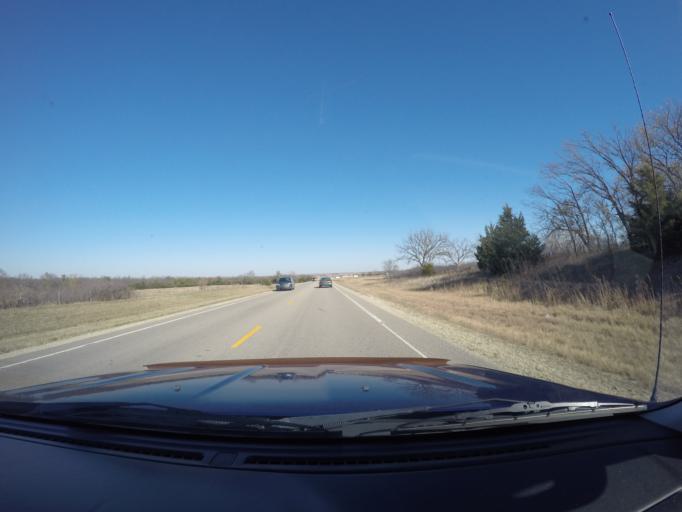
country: US
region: Kansas
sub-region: Marshall County
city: Blue Rapids
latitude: 39.4229
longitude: -96.7644
